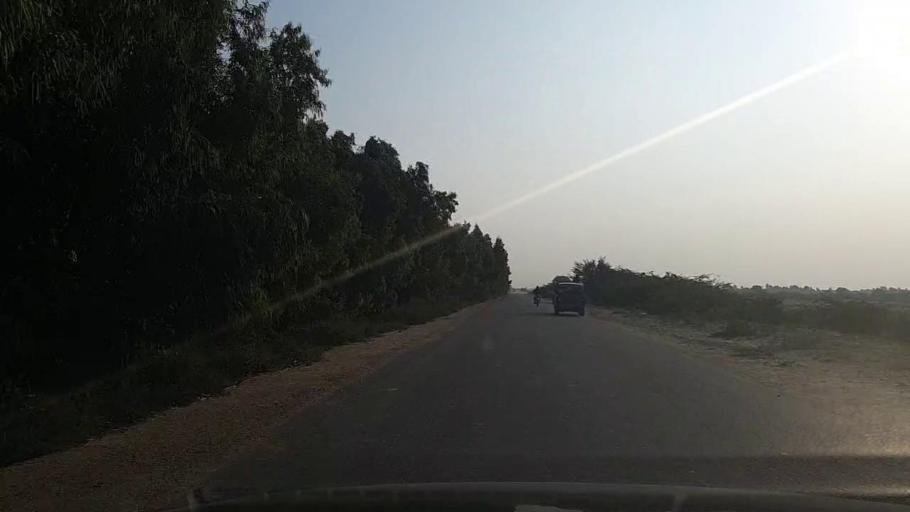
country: PK
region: Sindh
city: Mirpur Sakro
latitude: 24.4993
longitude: 67.8134
